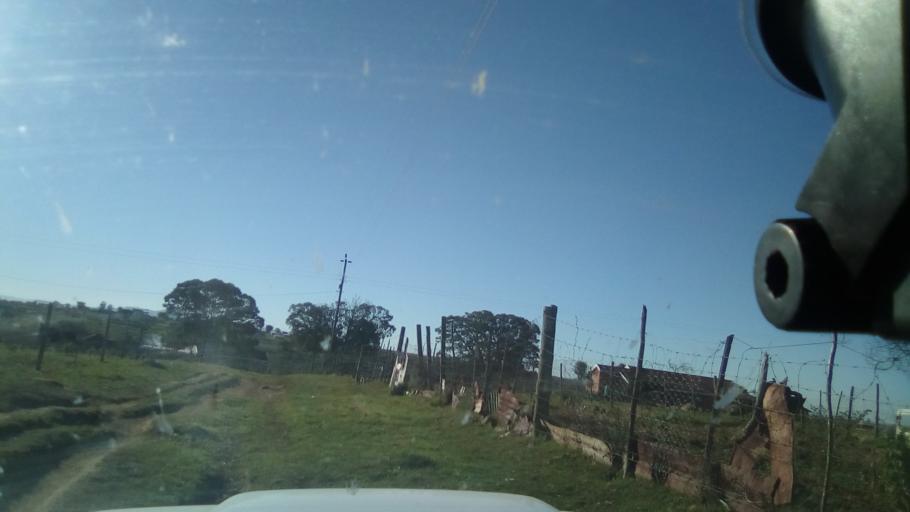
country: ZA
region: Eastern Cape
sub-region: Buffalo City Metropolitan Municipality
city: Bhisho
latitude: -32.9480
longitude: 27.2937
